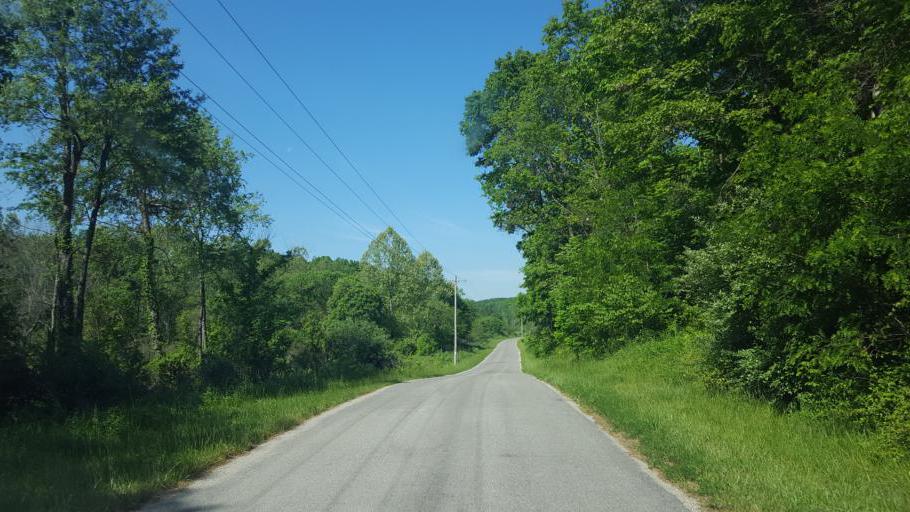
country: US
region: Ohio
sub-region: Jackson County
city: Wellston
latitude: 39.0025
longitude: -82.4776
